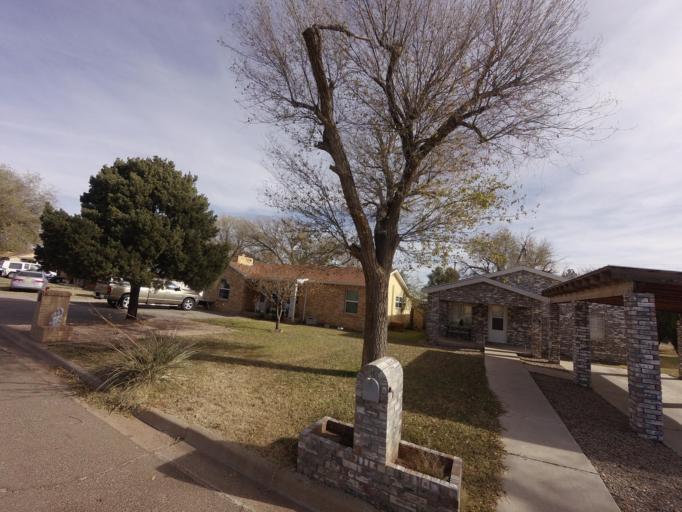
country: US
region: New Mexico
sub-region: Curry County
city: Clovis
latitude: 34.4112
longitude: -103.1940
